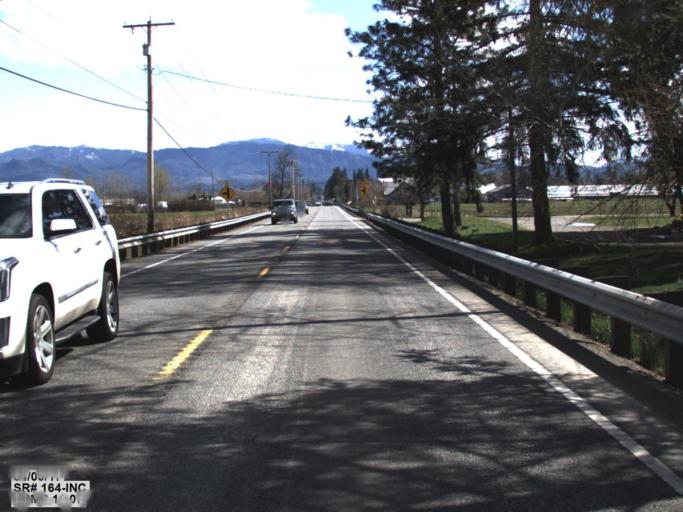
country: US
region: Washington
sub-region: Pierce County
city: Buckley
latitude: 47.2101
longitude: -122.0623
